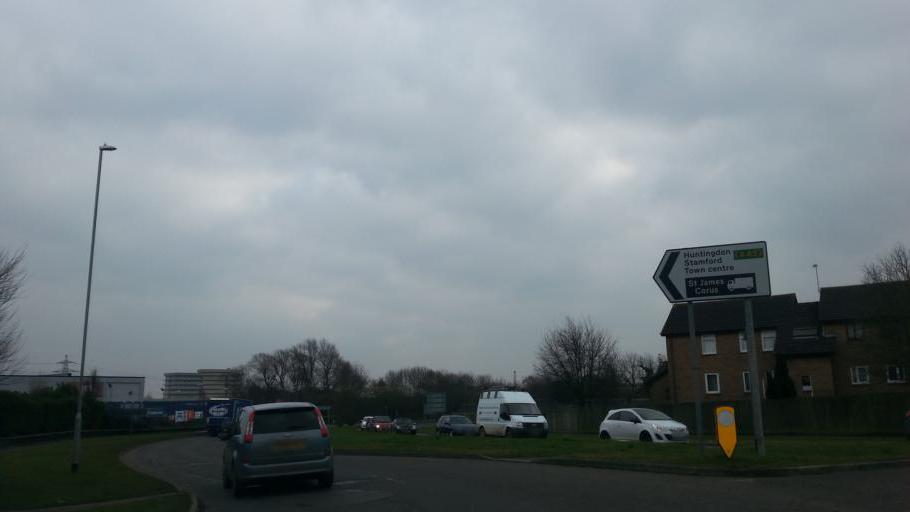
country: GB
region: England
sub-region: Northamptonshire
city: Corby
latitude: 52.4932
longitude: -0.6813
